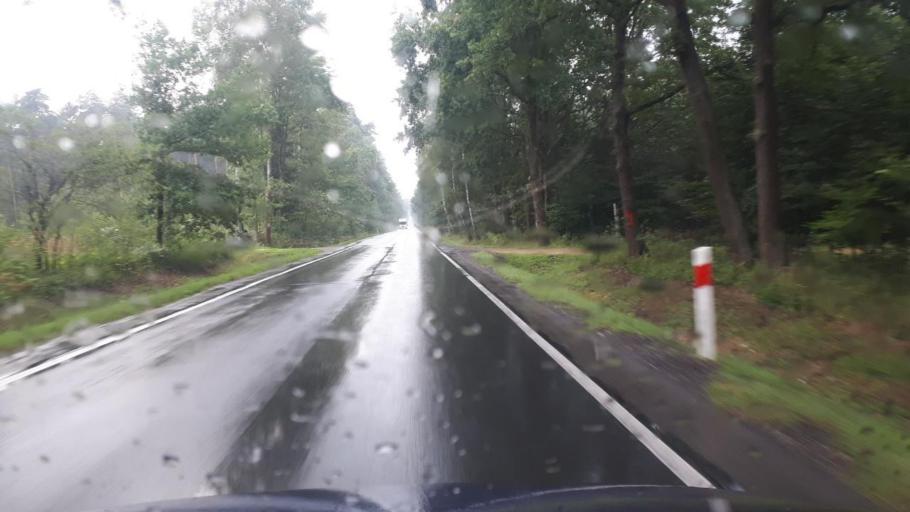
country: PL
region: Silesian Voivodeship
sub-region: Powiat tarnogorski
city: Tworog
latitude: 50.5299
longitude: 18.6807
